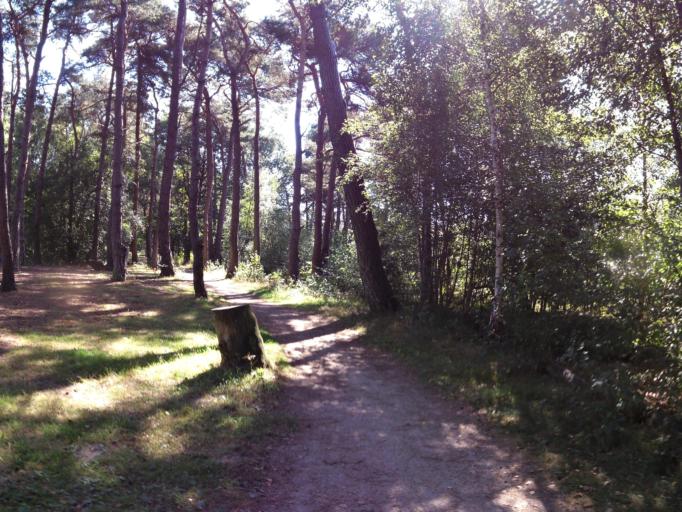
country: NL
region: Overijssel
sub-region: Gemeente Haaksbergen
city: Haaksbergen
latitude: 52.1524
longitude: 6.7983
